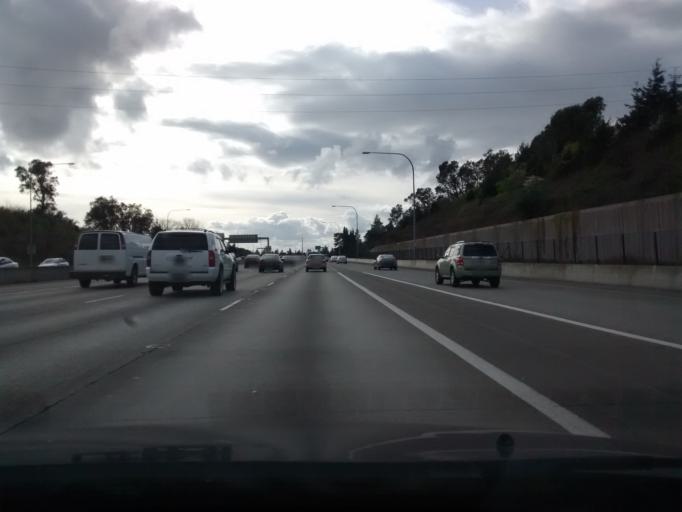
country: US
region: Washington
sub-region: Pierce County
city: Fircrest
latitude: 47.2350
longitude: -122.4874
